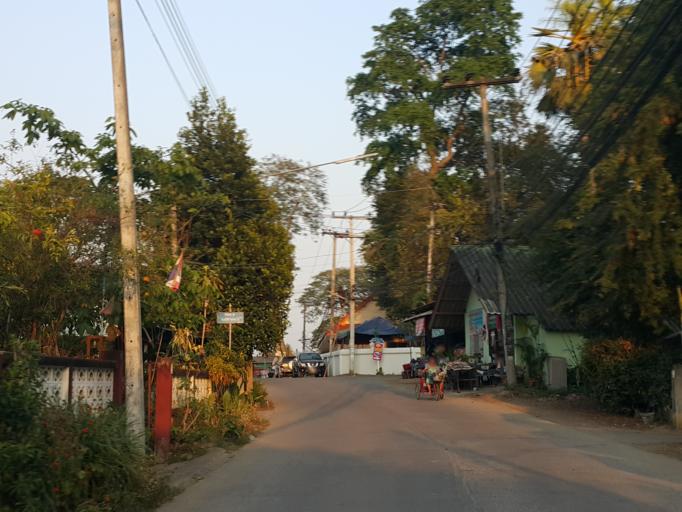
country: TH
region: Chiang Mai
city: San Sai
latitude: 18.8920
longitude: 98.9615
